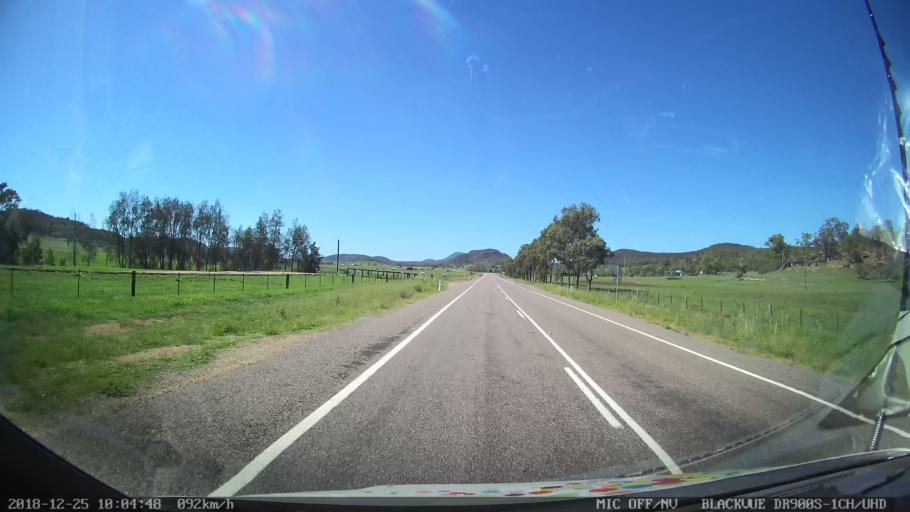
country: AU
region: New South Wales
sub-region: Upper Hunter Shire
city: Merriwa
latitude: -32.2387
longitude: 150.4860
